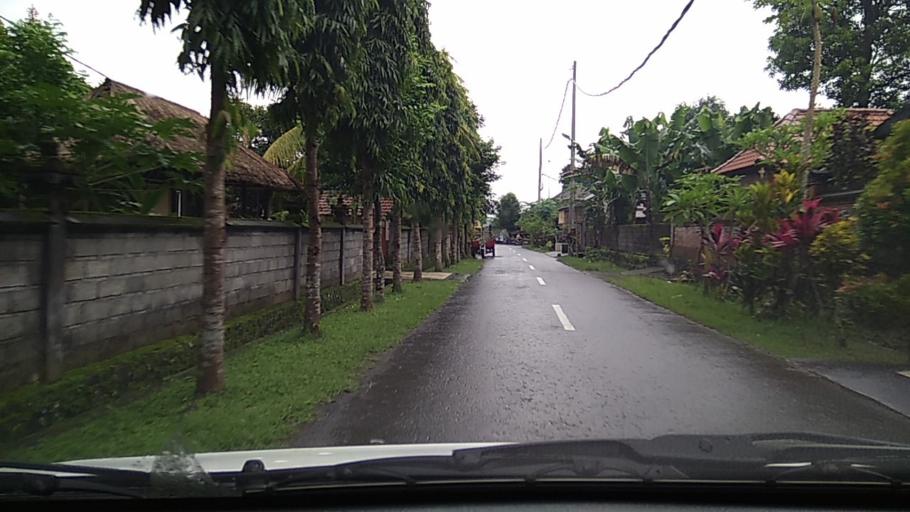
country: ID
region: Bali
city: Tiyingtali Kelod
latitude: -8.3995
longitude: 115.6194
